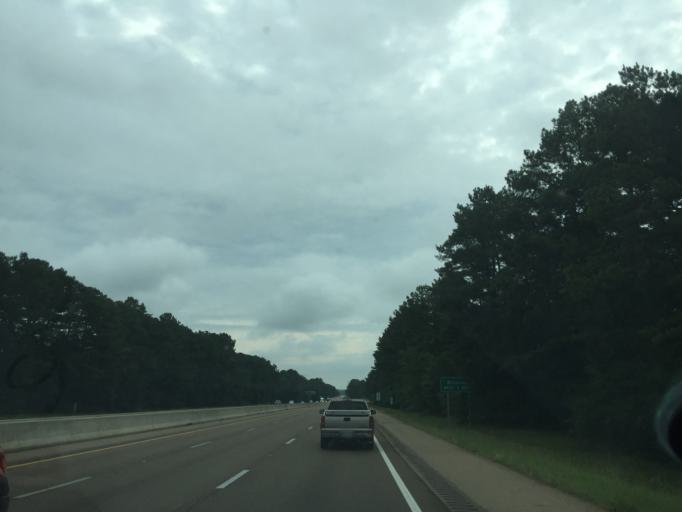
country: US
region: Mississippi
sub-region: Rankin County
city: Pearl
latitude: 32.2729
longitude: -90.0637
